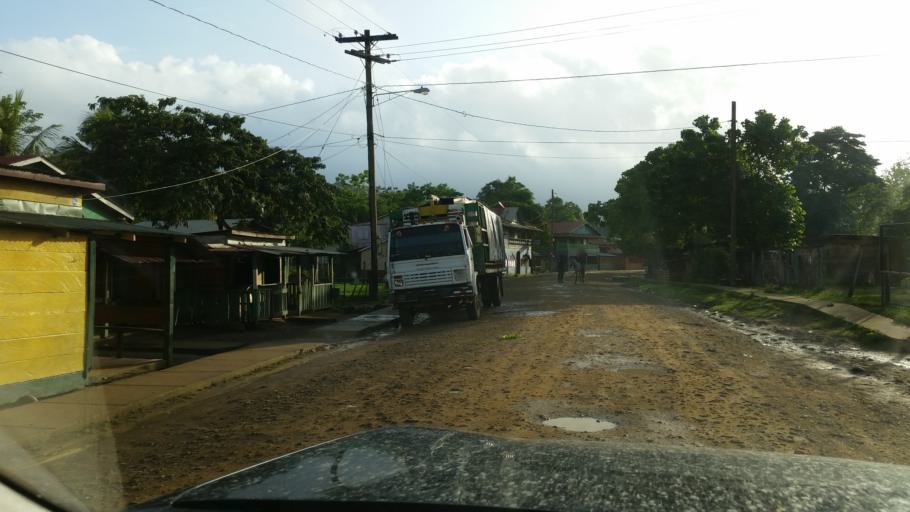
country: NI
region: Atlantico Norte (RAAN)
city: Puerto Cabezas
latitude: 14.0684
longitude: -83.9887
